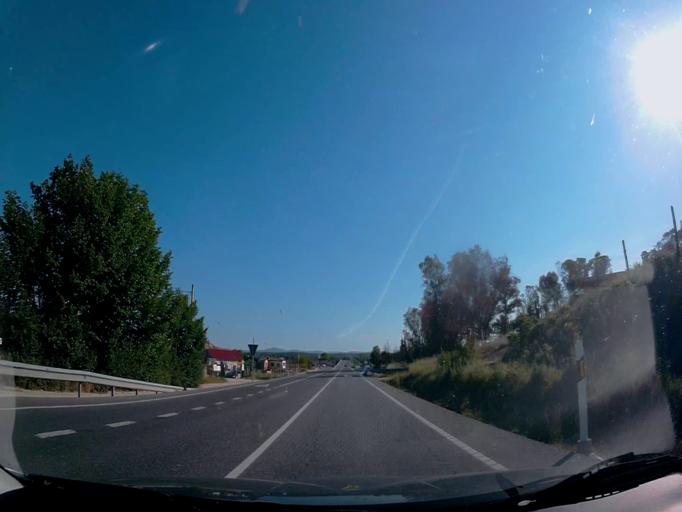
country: ES
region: Castille-La Mancha
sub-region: Province of Toledo
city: Escalona
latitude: 40.1551
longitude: -4.4017
